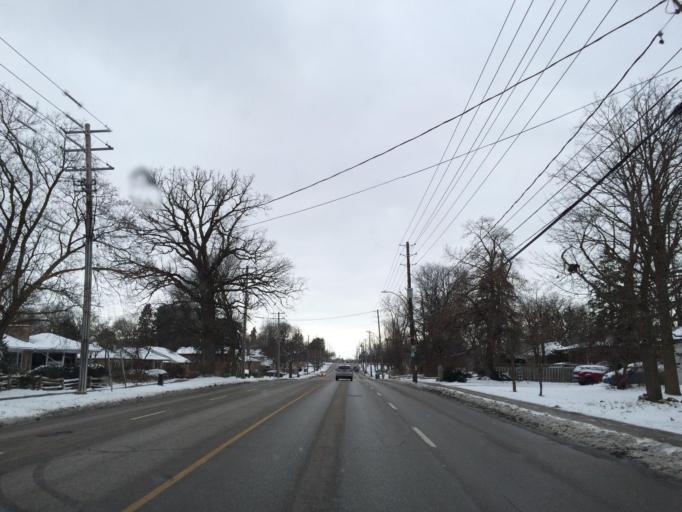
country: CA
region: Ontario
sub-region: Wellington County
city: Guelph
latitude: 43.5265
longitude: -80.2431
